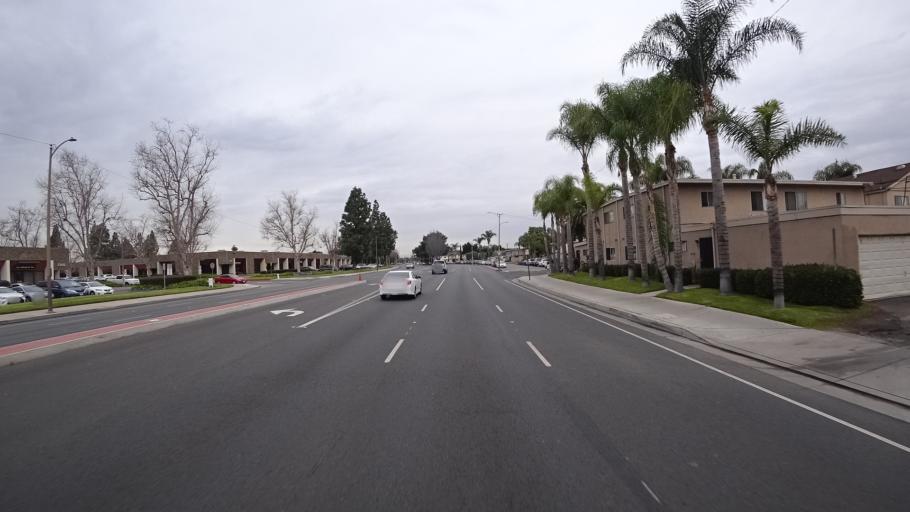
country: US
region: California
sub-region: Orange County
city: Fountain Valley
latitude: 33.7160
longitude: -117.9077
